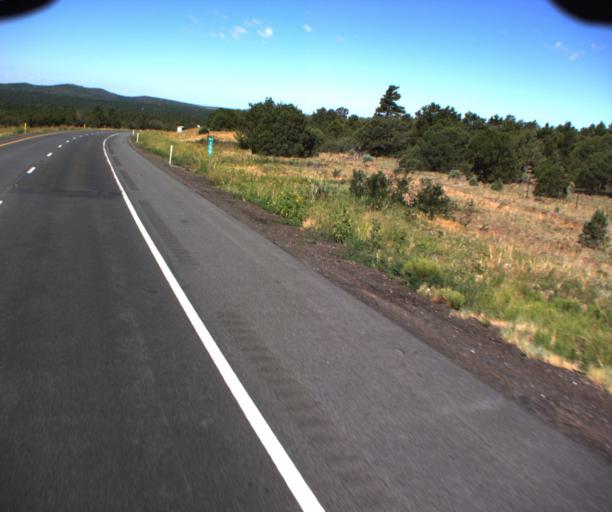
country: US
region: Arizona
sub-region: Coconino County
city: Williams
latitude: 35.2235
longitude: -112.2551
